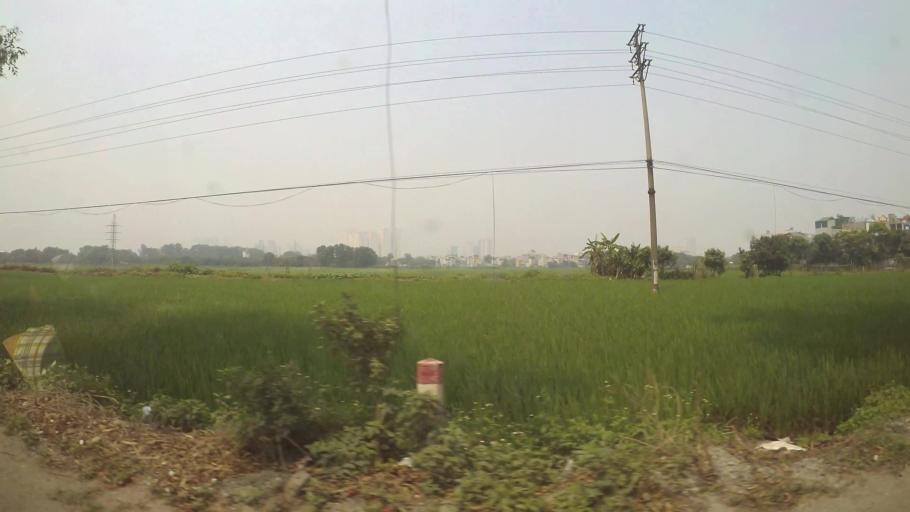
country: VN
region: Ha Noi
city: Van Dien
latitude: 20.9495
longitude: 105.8225
